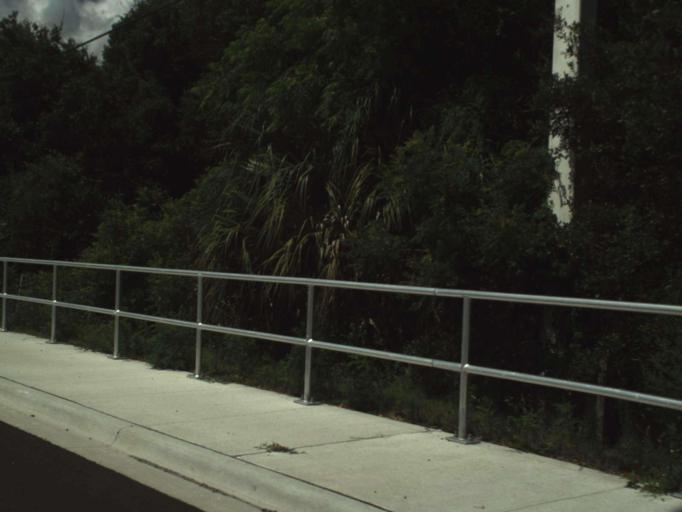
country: US
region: Florida
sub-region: Seminole County
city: Midway
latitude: 28.8603
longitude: -81.1623
